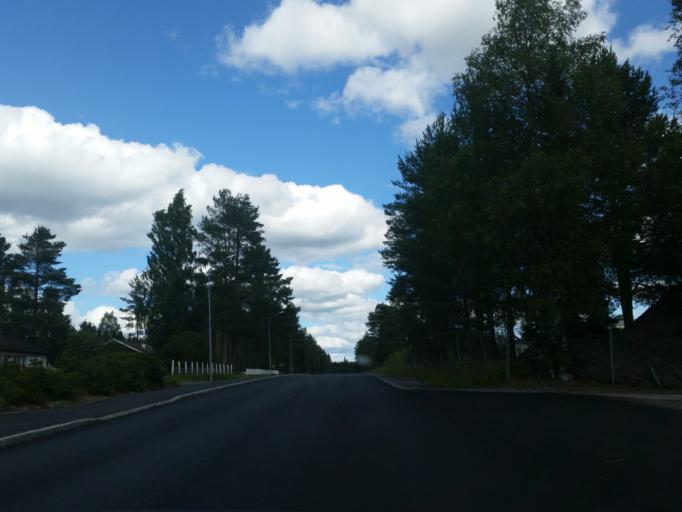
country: SE
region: Vaesterbotten
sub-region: Robertsfors Kommun
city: Robertsfors
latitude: 64.1970
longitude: 20.8455
